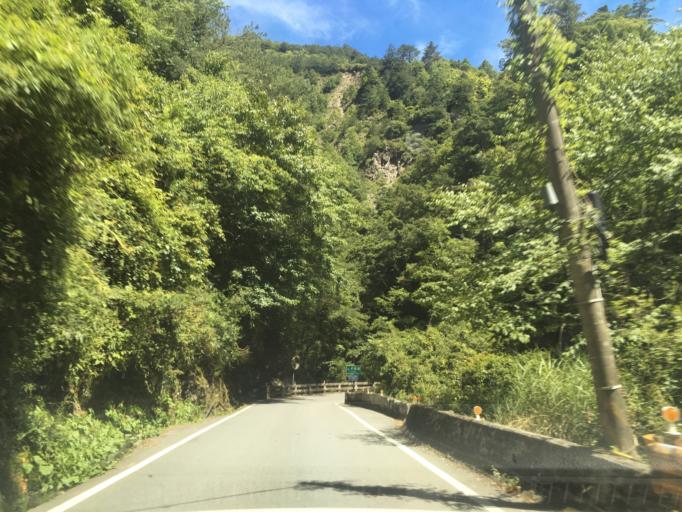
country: TW
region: Taiwan
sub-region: Nantou
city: Puli
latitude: 24.2124
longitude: 121.2653
